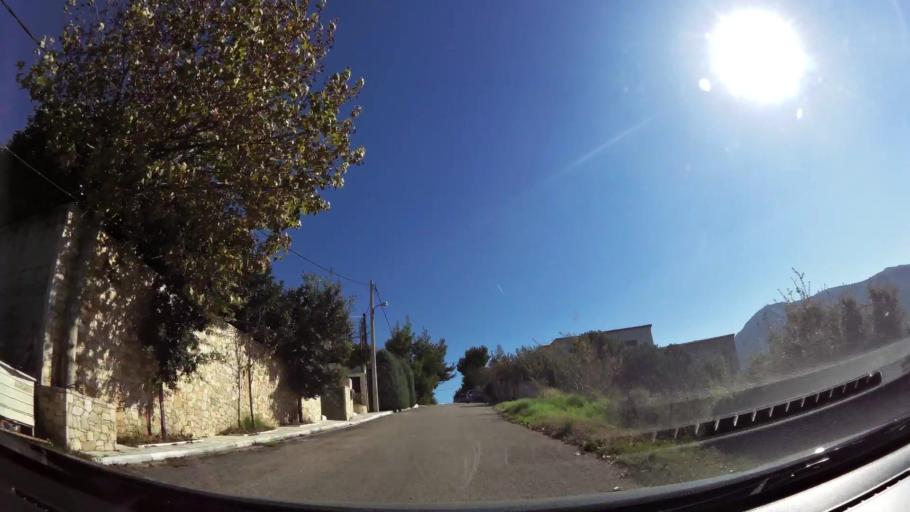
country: GR
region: Attica
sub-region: Nomarchia Anatolikis Attikis
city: Rodopoli
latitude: 38.1111
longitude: 23.8845
